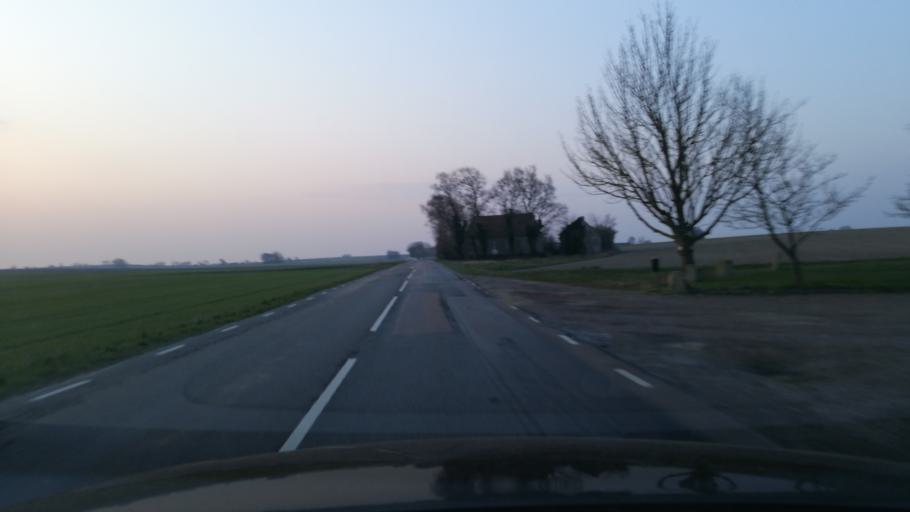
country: SE
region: Skane
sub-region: Ystads Kommun
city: Kopingebro
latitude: 55.4582
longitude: 14.1089
